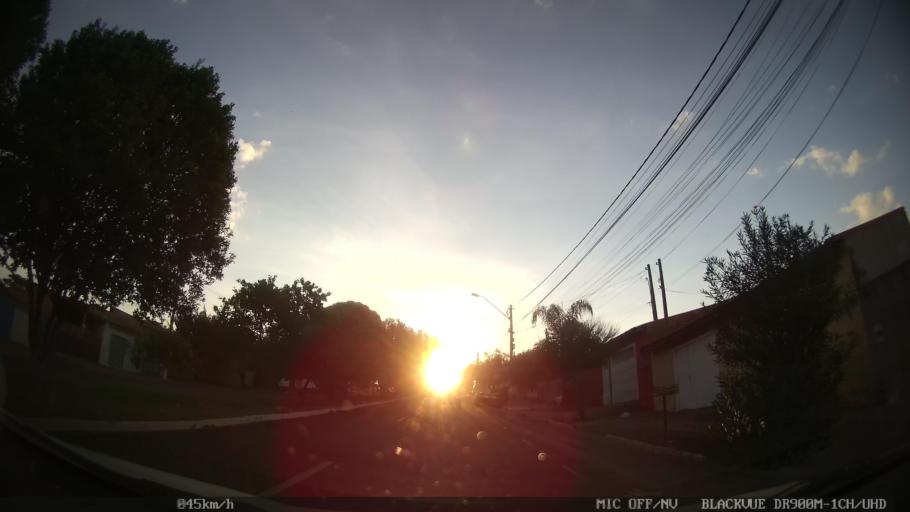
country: BR
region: Sao Paulo
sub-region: Ribeirao Preto
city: Ribeirao Preto
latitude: -21.1497
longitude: -47.8471
